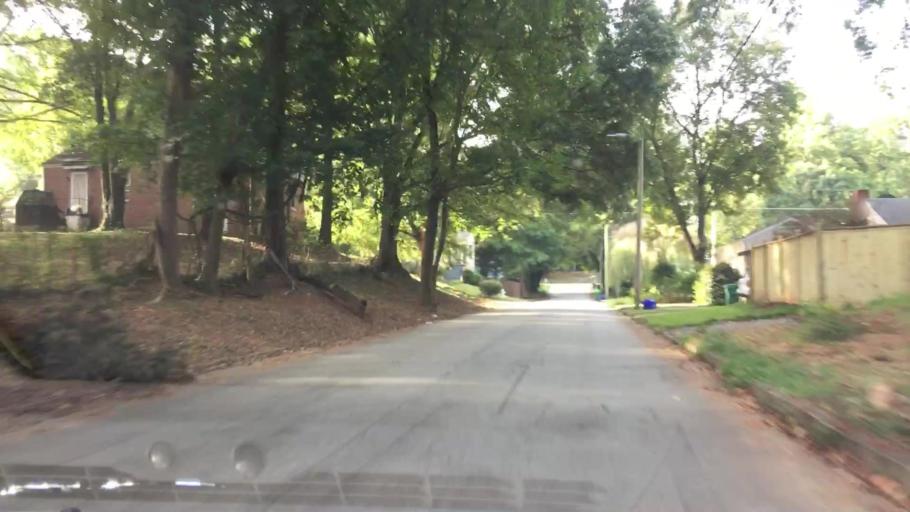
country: US
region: Georgia
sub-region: DeKalb County
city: Gresham Park
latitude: 33.7398
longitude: -84.3182
